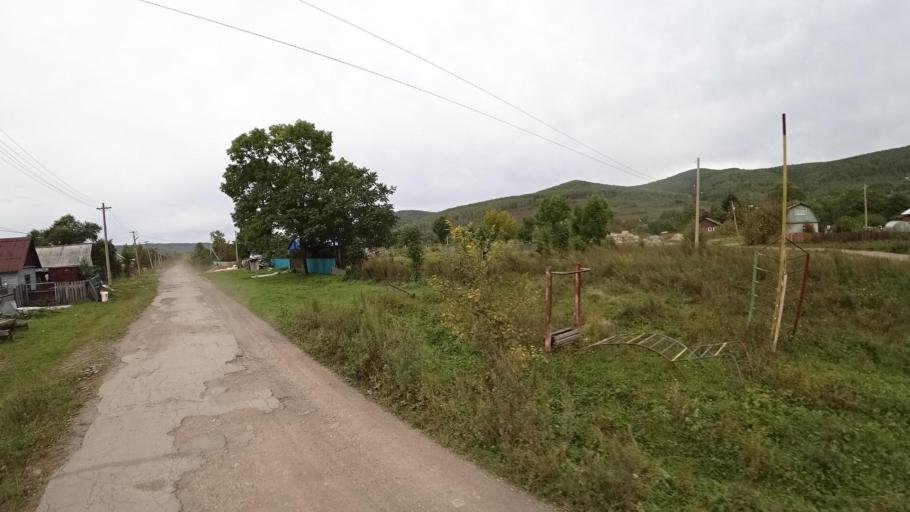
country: RU
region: Jewish Autonomous Oblast
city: Khingansk
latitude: 49.0378
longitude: 131.0496
